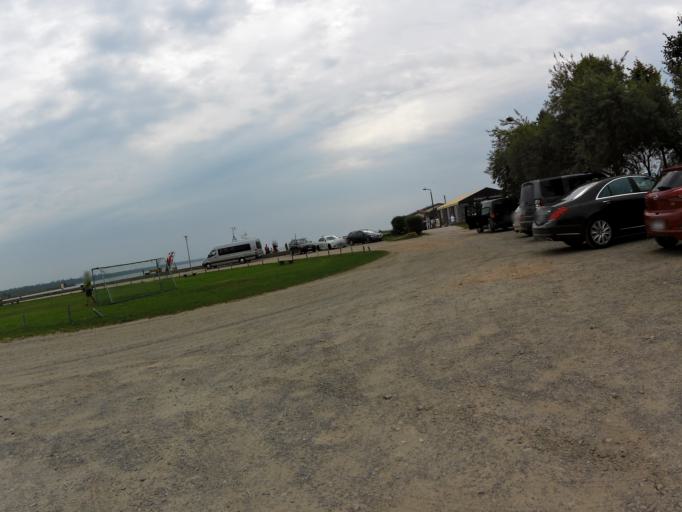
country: PL
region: West Pomeranian Voivodeship
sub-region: Swinoujscie
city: Swinoujscie
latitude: 53.8676
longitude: 14.2050
